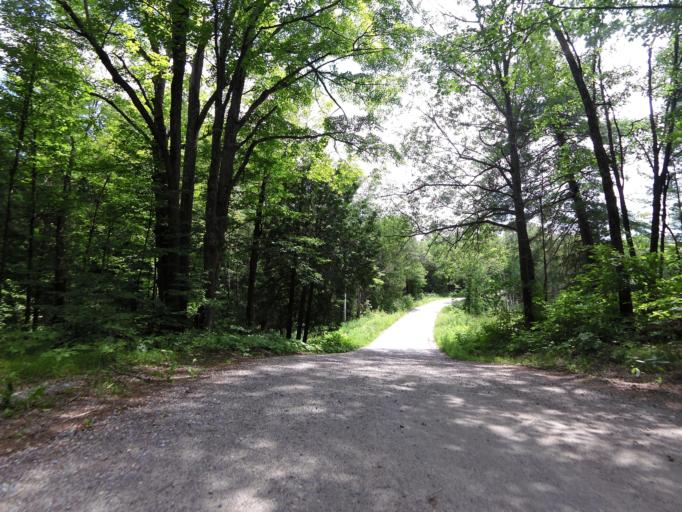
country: CA
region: Ontario
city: Perth
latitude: 44.7840
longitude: -76.6102
